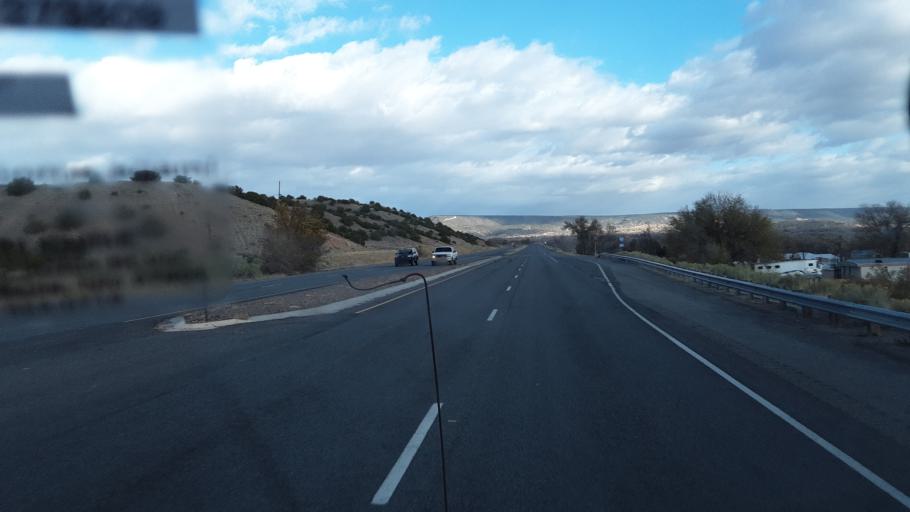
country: US
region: New Mexico
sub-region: Rio Arriba County
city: Ohkay Owingeh
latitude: 36.0287
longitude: -106.0931
